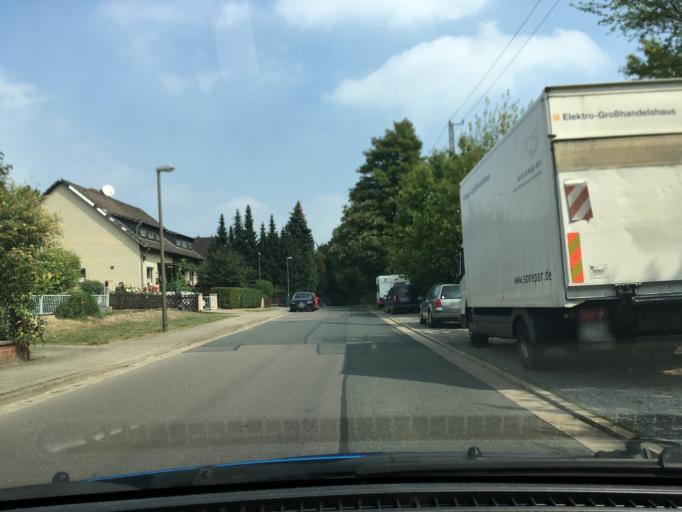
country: DE
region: Lower Saxony
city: Langenhagen
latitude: 52.4460
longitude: 9.7314
